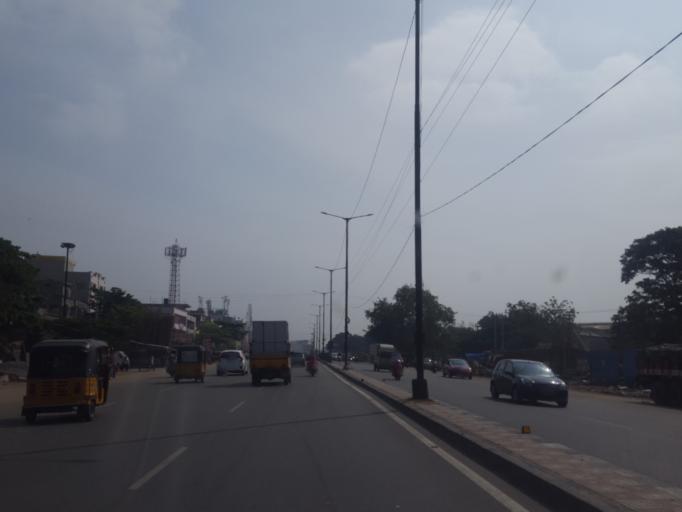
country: IN
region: Telangana
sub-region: Medak
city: Serilingampalle
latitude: 17.5057
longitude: 78.3064
